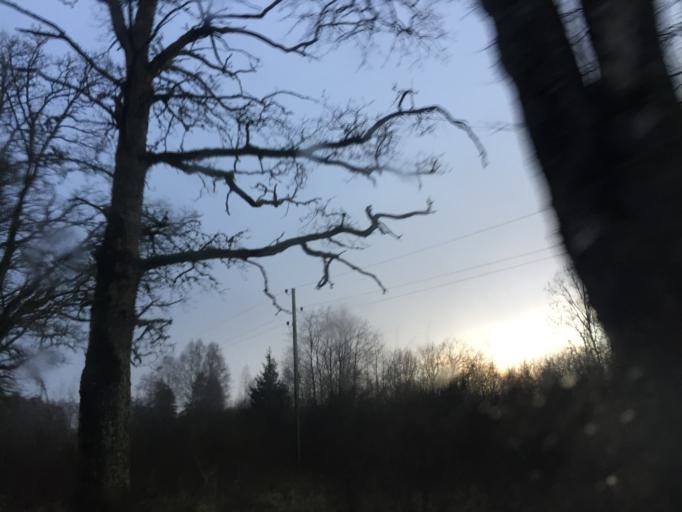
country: LV
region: Burtnieki
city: Matisi
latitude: 57.6889
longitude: 25.2550
